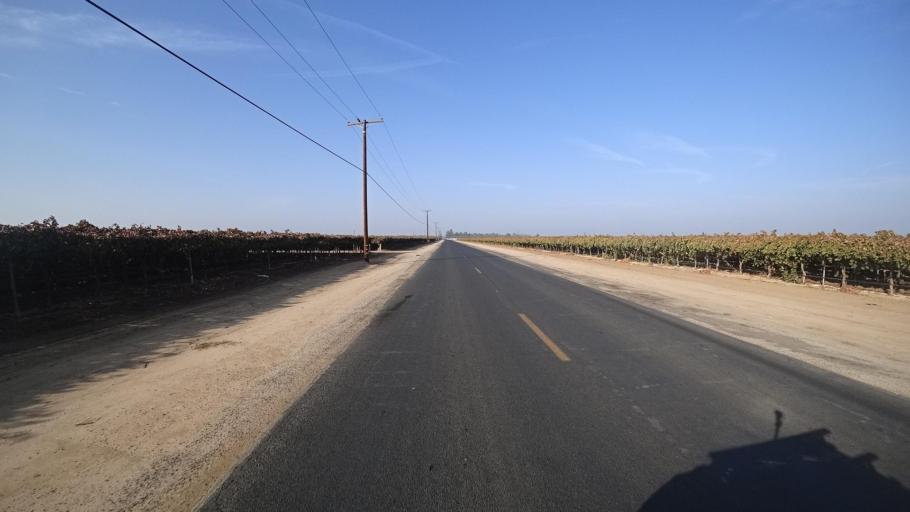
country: US
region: California
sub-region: Kern County
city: McFarland
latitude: 35.6746
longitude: -119.2005
